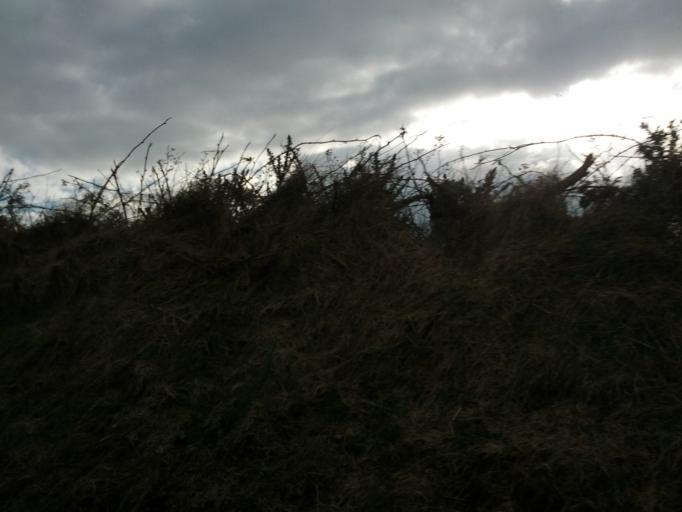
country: IE
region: Connaught
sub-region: County Galway
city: Athenry
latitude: 53.4286
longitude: -8.6223
